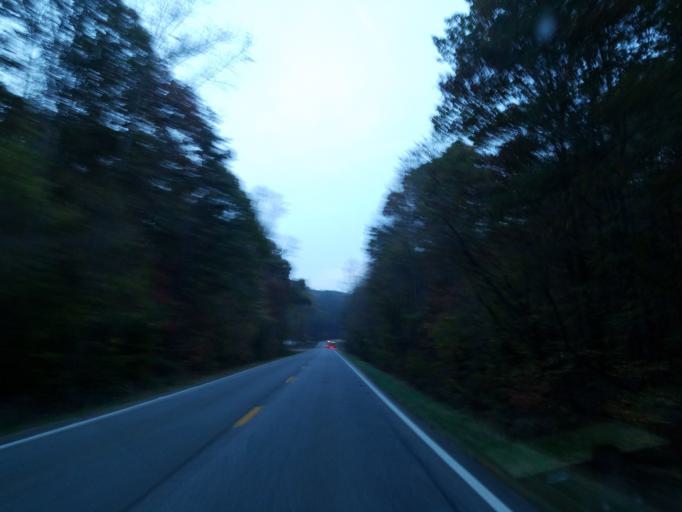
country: US
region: Georgia
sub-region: Pickens County
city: Jasper
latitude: 34.5338
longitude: -84.5732
